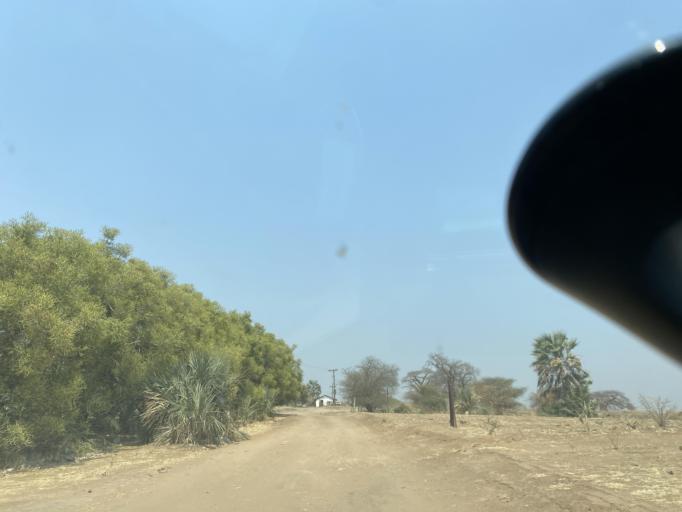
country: ZW
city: Chirundu
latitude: -16.1594
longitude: 28.8056
